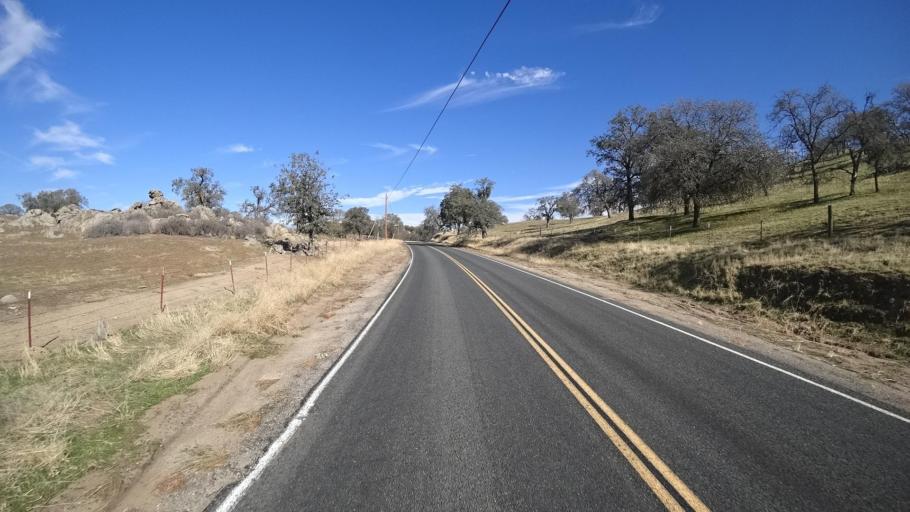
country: US
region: California
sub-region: Kern County
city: Oildale
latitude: 35.6249
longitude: -118.8431
